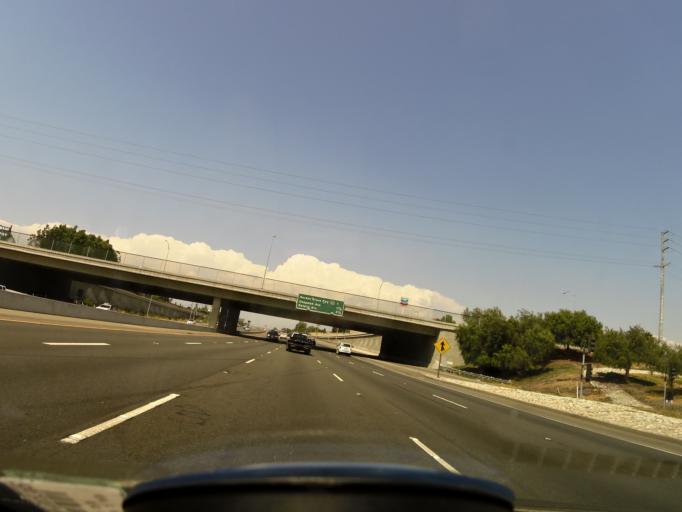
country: US
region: California
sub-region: Orange County
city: Tustin
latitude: 33.7588
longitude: -117.8310
